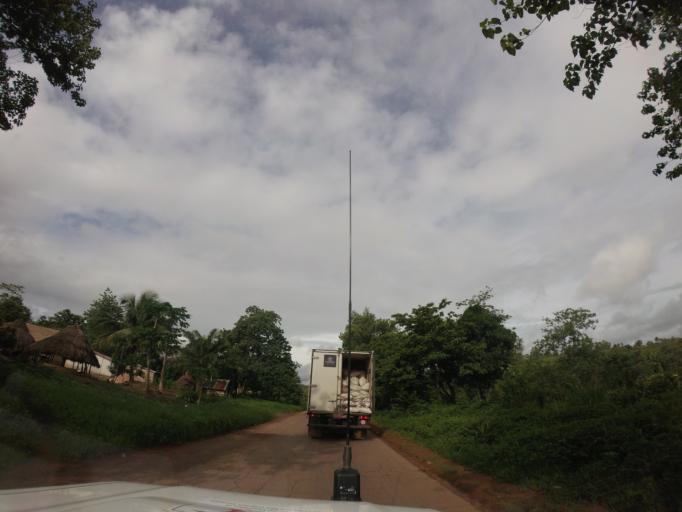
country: GN
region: Kindia
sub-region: Coyah
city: Coyah
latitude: 9.8106
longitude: -13.2729
